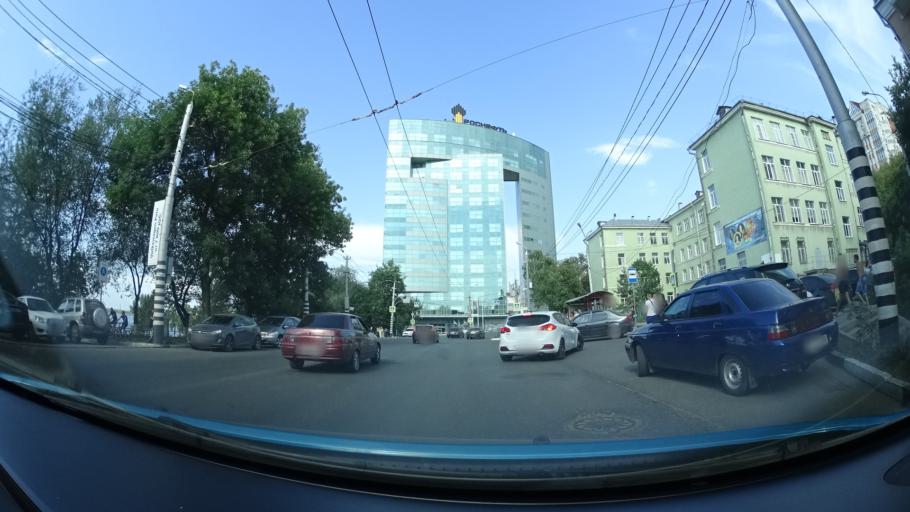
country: RU
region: Samara
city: Samara
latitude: 53.2106
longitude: 50.1215
